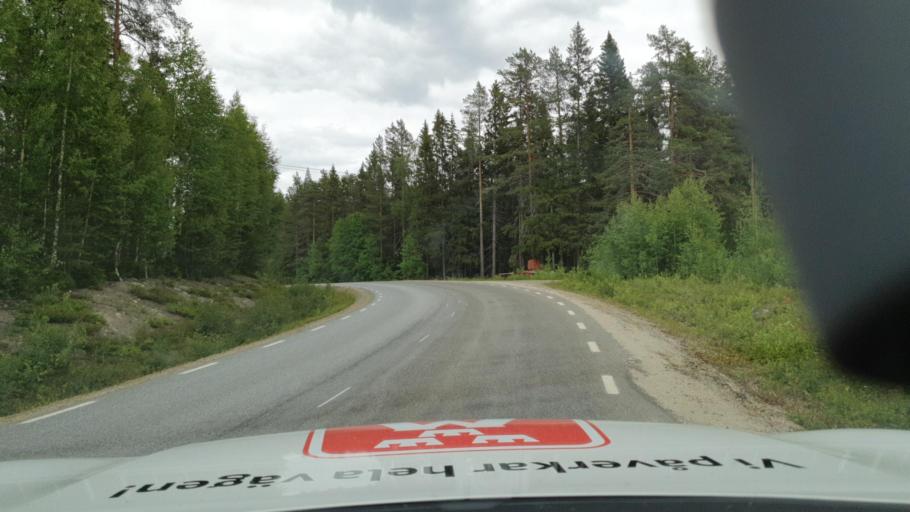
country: SE
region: Vaesterbotten
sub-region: Bjurholms Kommun
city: Bjurholm
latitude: 63.8675
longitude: 18.9678
